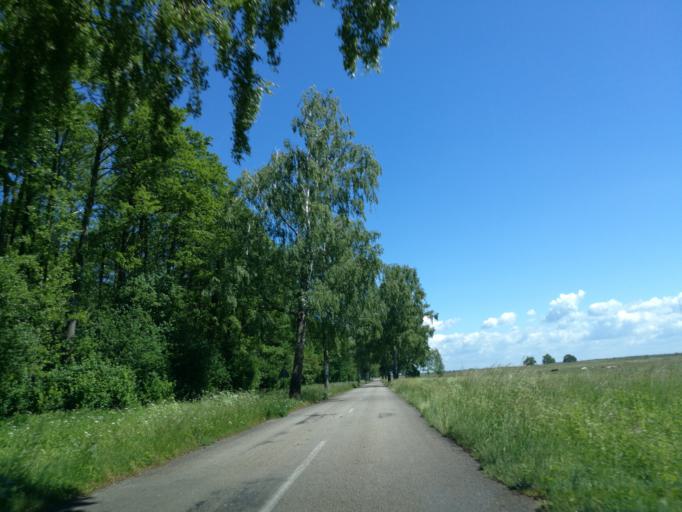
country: LT
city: Rusne
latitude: 55.3843
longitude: 21.2347
